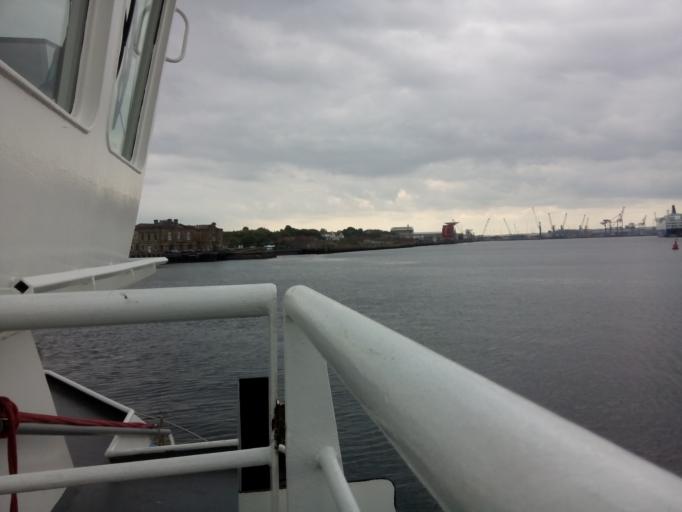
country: GB
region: England
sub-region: South Tyneside
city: South Shields
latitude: 54.9973
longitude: -1.4415
